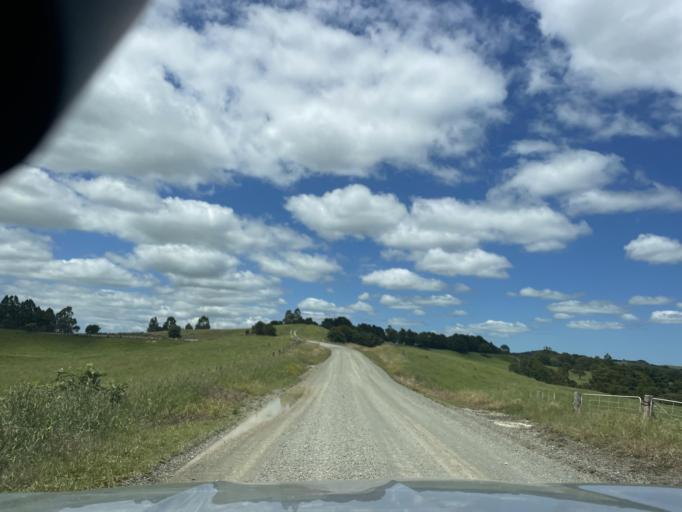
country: NZ
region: Auckland
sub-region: Auckland
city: Wellsford
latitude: -36.1597
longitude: 174.5302
